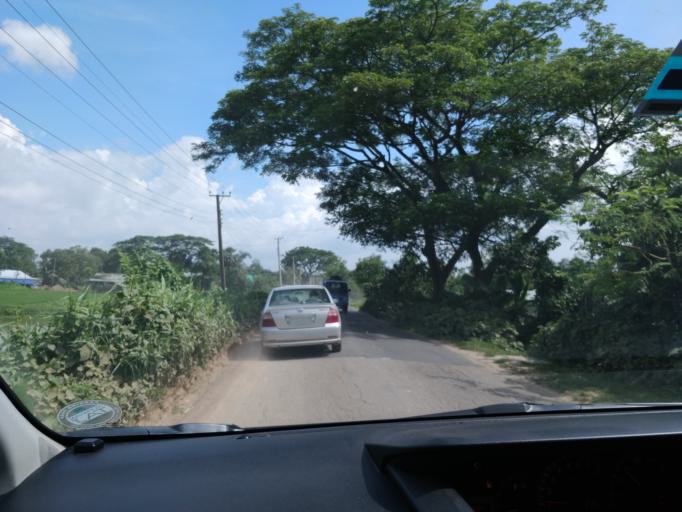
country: BD
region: Dhaka
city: Bhairab Bazar
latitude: 24.1060
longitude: 91.1253
